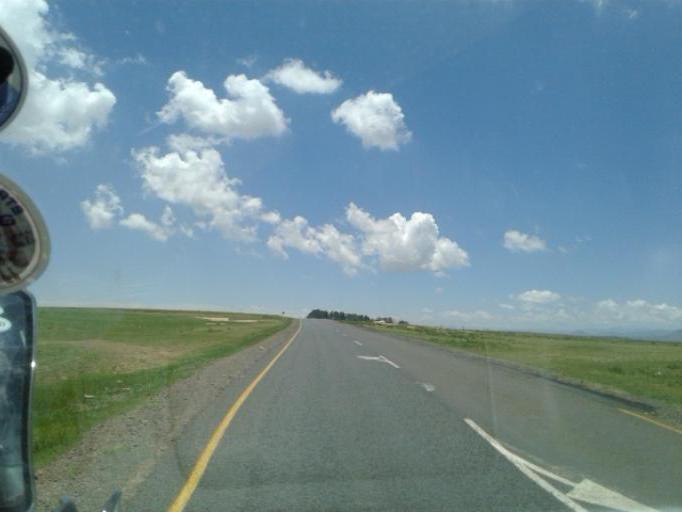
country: LS
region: Maseru
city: Maseru
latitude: -29.2991
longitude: 27.6140
